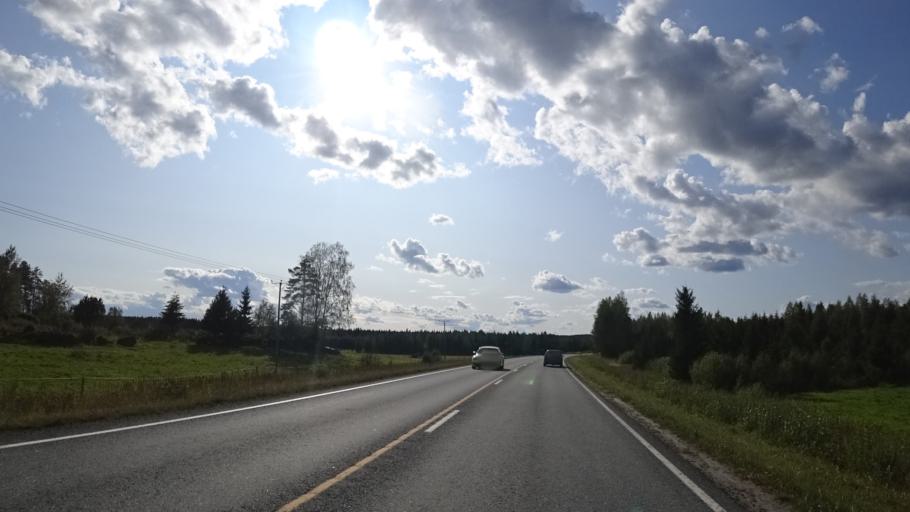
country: FI
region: North Karelia
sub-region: Keski-Karjala
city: Kitee
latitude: 62.0884
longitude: 30.0013
